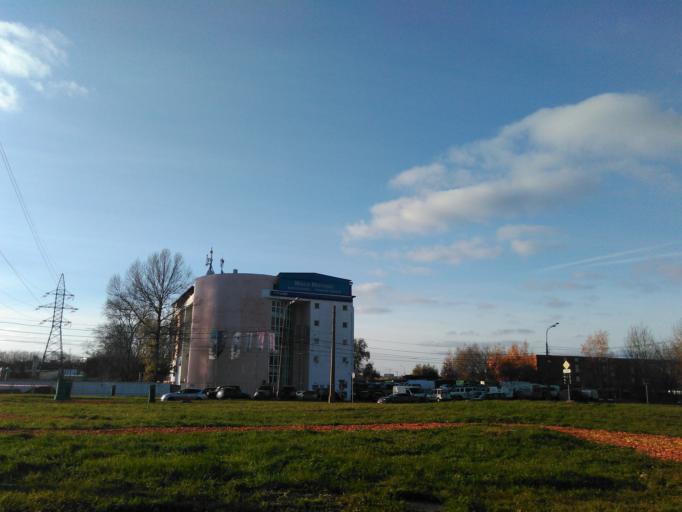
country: RU
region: Moscow
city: Mar'ina Roshcha
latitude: 55.8124
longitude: 37.6196
